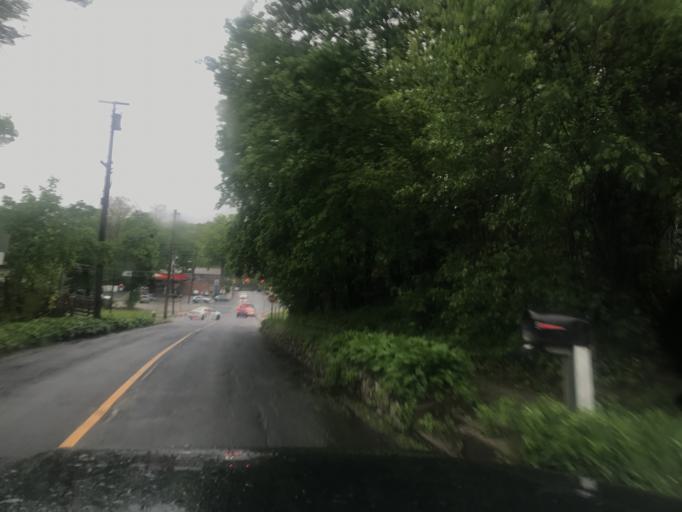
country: US
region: Connecticut
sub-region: Fairfield County
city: Bethel
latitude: 41.3704
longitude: -73.4071
